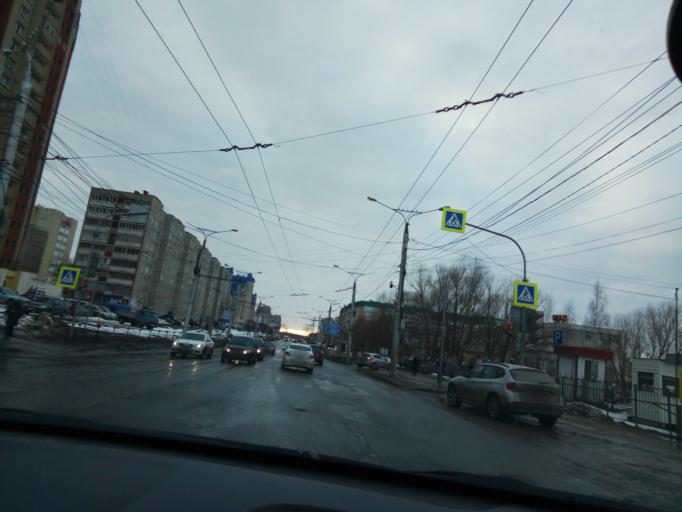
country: RU
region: Chuvashia
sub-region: Cheboksarskiy Rayon
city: Cheboksary
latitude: 56.1488
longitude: 47.1859
